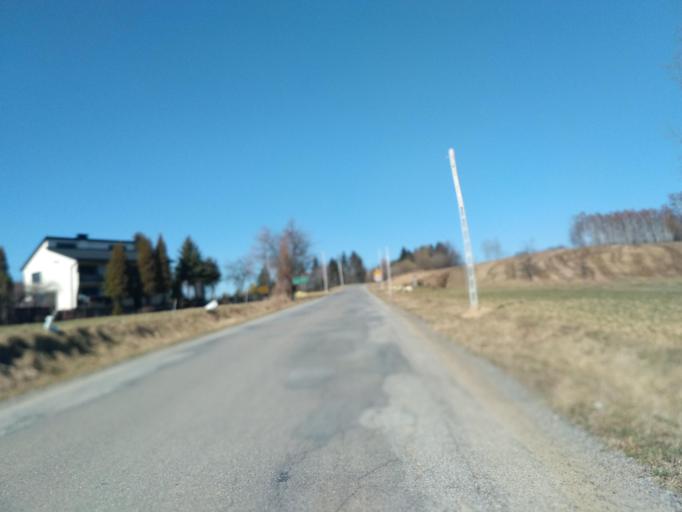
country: PL
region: Subcarpathian Voivodeship
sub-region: Powiat debicki
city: Brzostek
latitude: 49.9463
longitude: 21.4312
